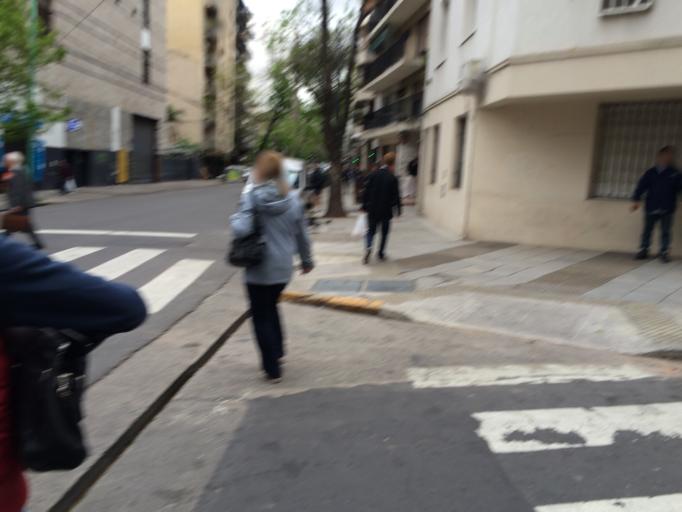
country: AR
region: Buenos Aires F.D.
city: Retiro
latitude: -34.5904
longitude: -58.4055
